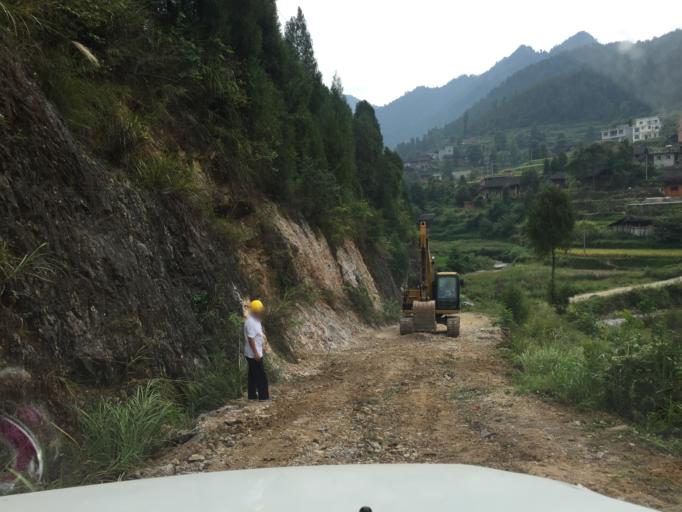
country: CN
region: Guizhou Sheng
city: Dabachang
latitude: 27.7980
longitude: 108.4022
